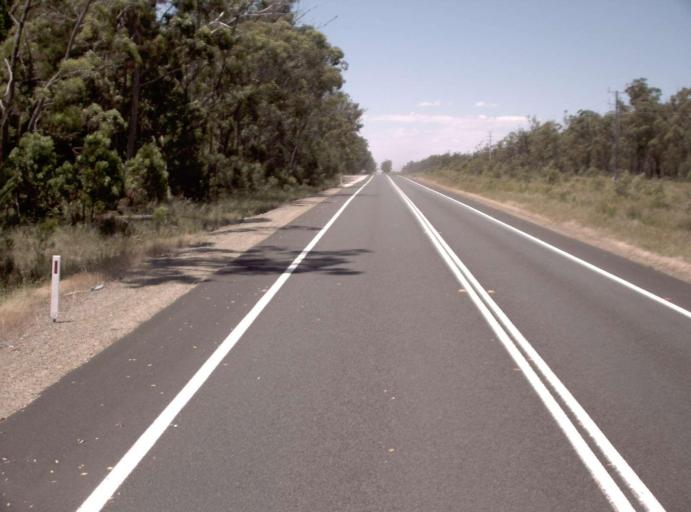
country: AU
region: Victoria
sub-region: East Gippsland
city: Lakes Entrance
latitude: -37.7559
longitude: 148.3031
